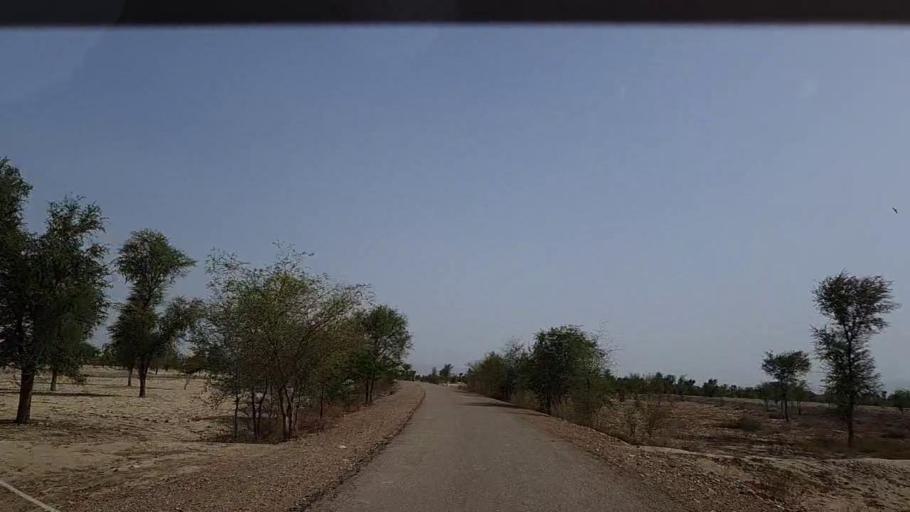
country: PK
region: Sindh
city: Johi
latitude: 26.6332
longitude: 67.5017
